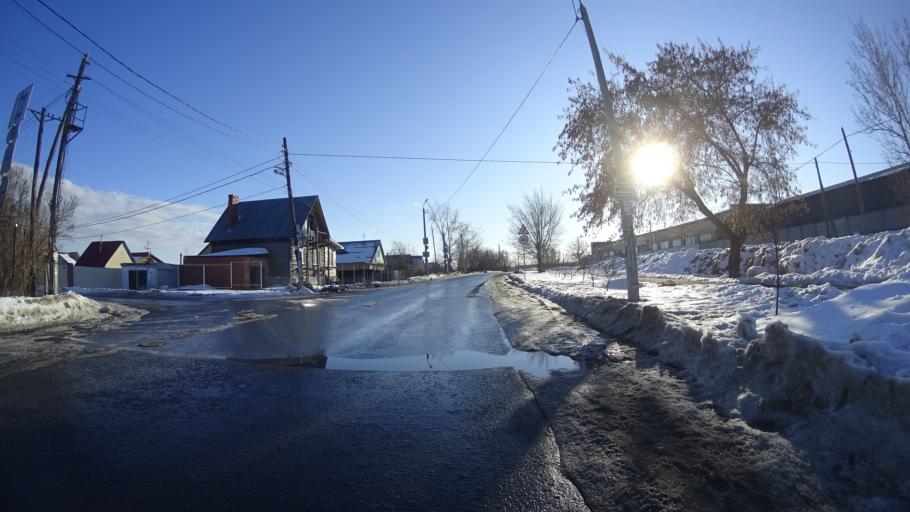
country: RU
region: Chelyabinsk
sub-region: Gorod Chelyabinsk
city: Chelyabinsk
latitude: 55.1498
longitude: 61.3077
